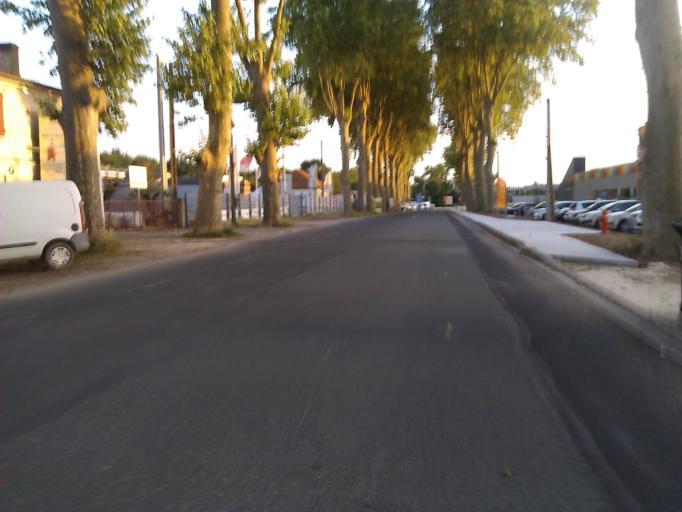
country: FR
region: Aquitaine
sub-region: Departement de la Gironde
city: Carbon-Blanc
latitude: 44.9005
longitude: -0.4927
